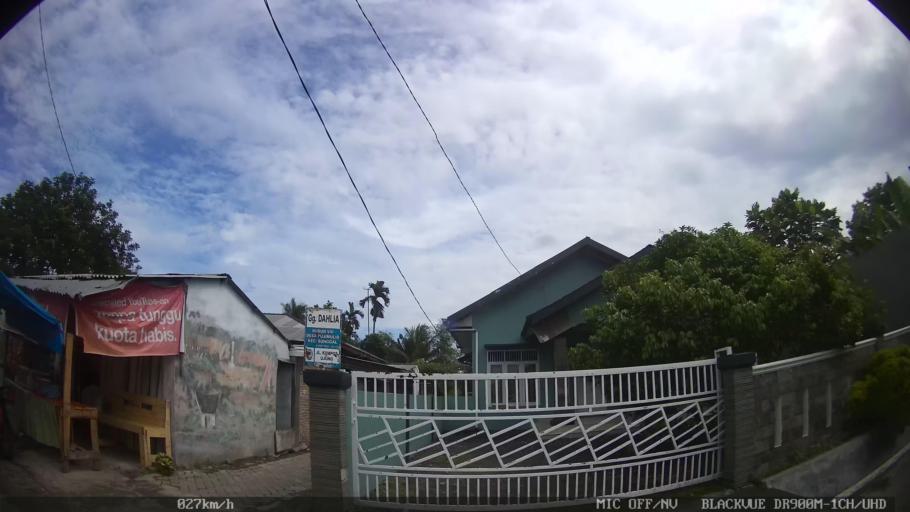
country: ID
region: North Sumatra
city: Sunggal
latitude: 3.5866
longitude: 98.5821
